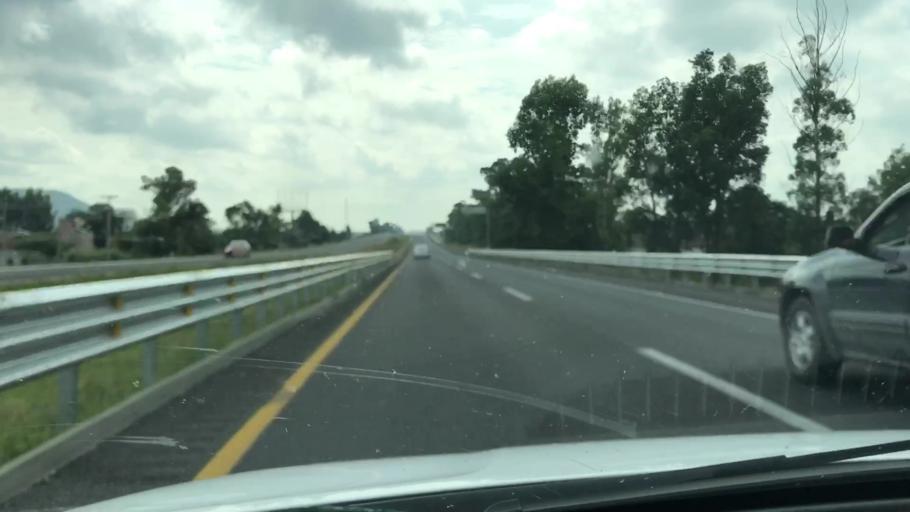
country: MX
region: Guanajuato
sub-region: Salamanca
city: El Divisador
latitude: 20.5951
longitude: -101.1673
